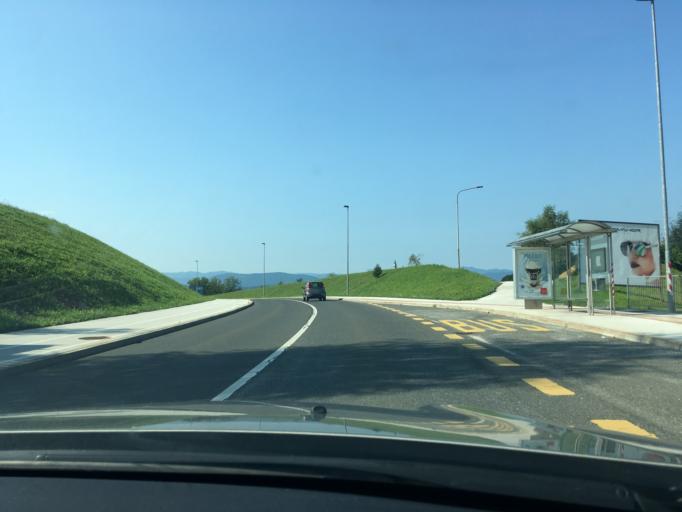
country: SI
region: Novo Mesto
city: Novo Mesto
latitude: 45.8276
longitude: 15.1563
